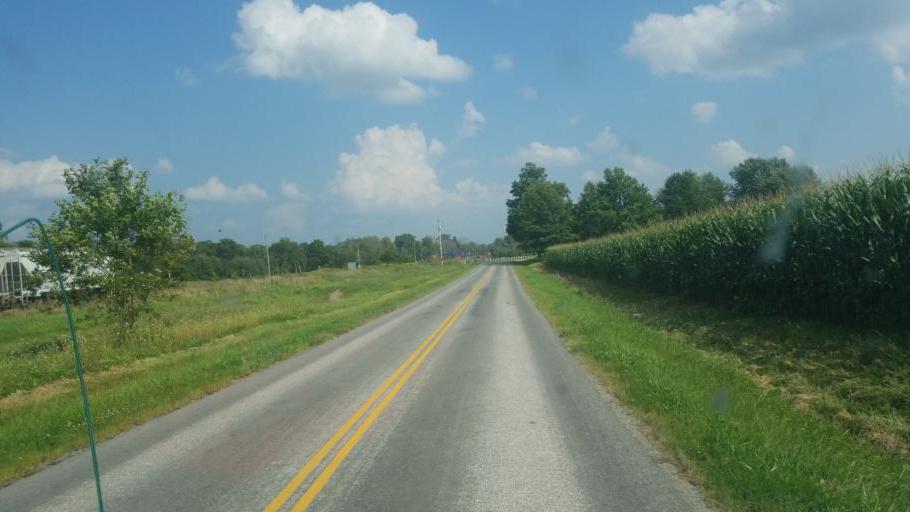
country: US
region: Ohio
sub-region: Wayne County
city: West Salem
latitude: 41.0433
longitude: -82.1471
